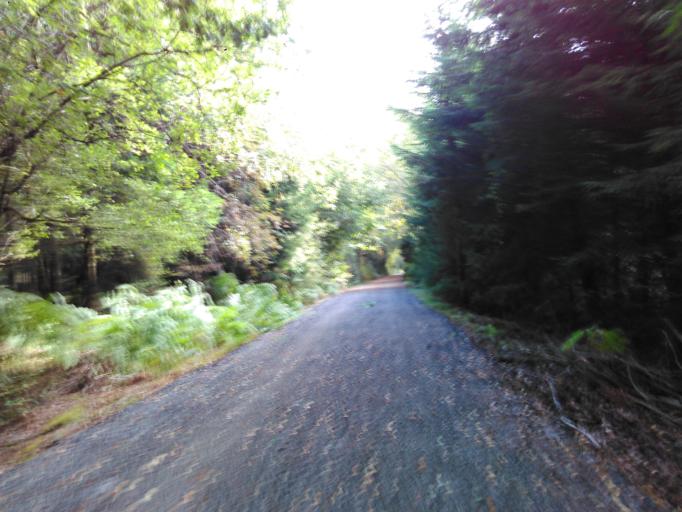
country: BE
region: Wallonia
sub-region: Province du Luxembourg
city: Vaux-sur-Sure
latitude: 49.9364
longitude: 5.5305
